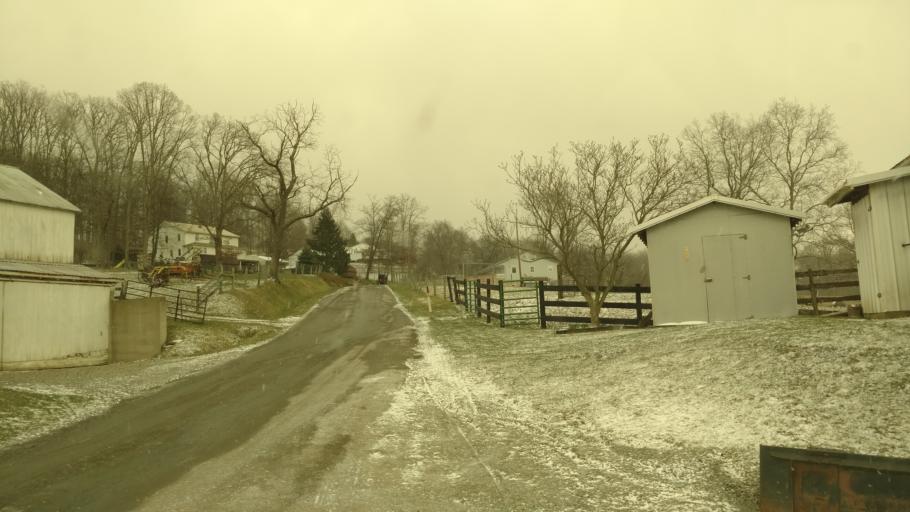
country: US
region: Ohio
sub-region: Coshocton County
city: West Lafayette
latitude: 40.4323
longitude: -81.7952
